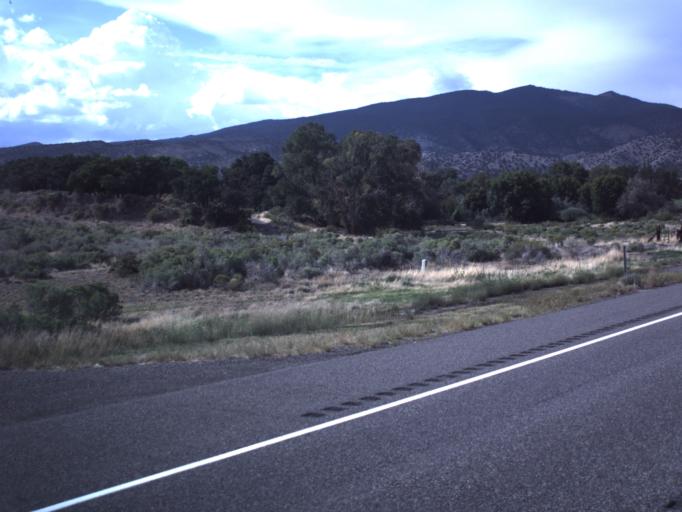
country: US
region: Utah
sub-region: Sevier County
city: Monroe
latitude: 38.5812
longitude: -112.2581
